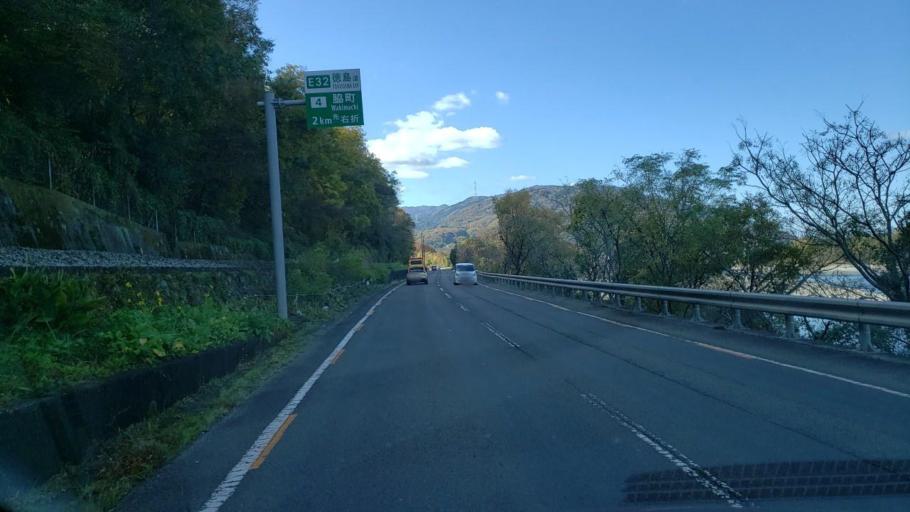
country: JP
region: Tokushima
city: Wakimachi
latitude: 34.0592
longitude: 134.1847
